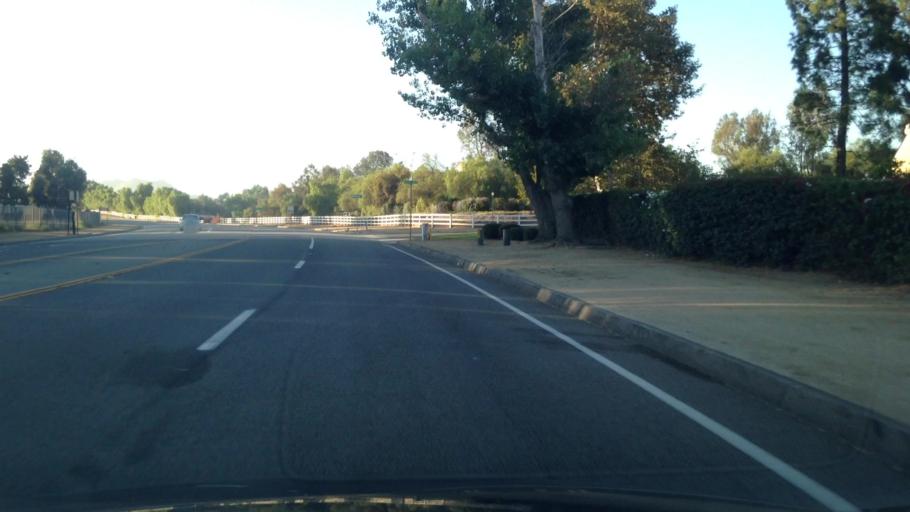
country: US
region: California
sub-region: Riverside County
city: Woodcrest
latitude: 33.8509
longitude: -117.3661
